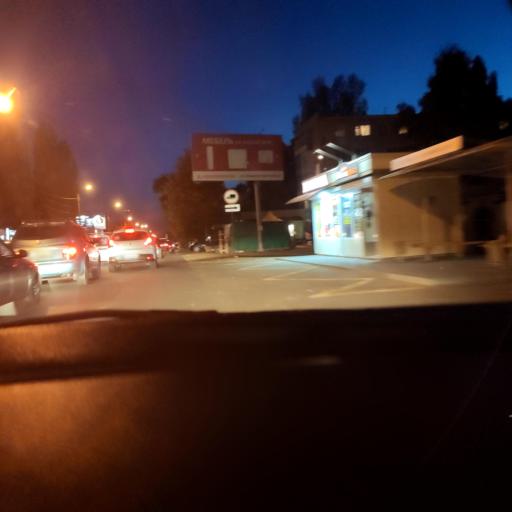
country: RU
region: Voronezj
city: Voronezh
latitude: 51.6757
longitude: 39.1568
